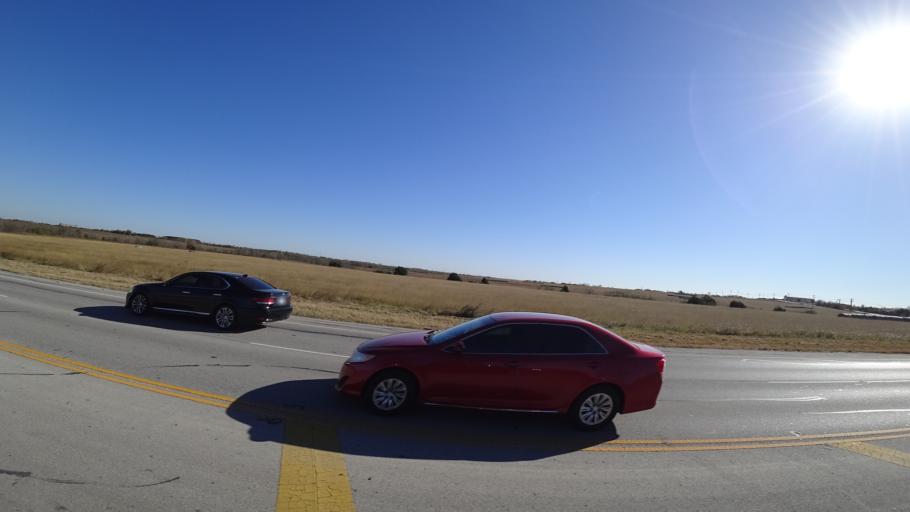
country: US
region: Texas
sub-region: Travis County
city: Onion Creek
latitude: 30.1462
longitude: -97.6969
